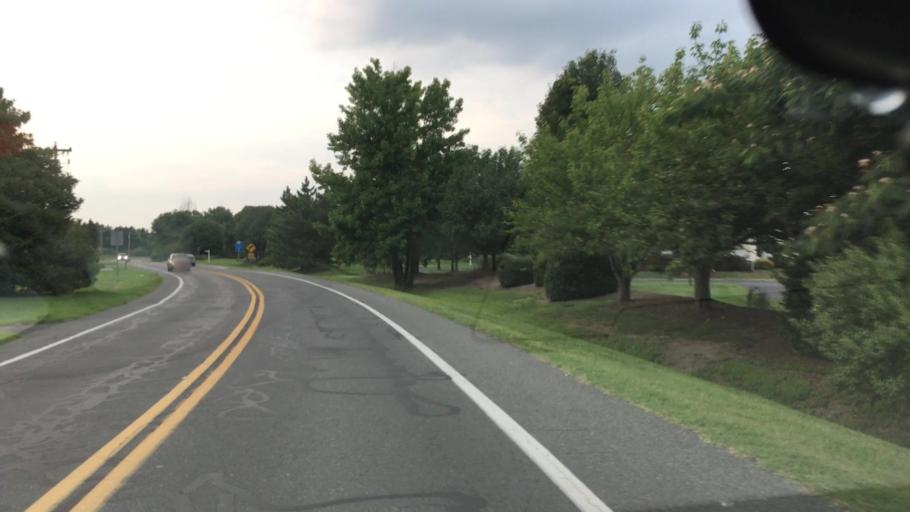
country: US
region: Delaware
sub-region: Sussex County
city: Ocean View
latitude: 38.5311
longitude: -75.0867
